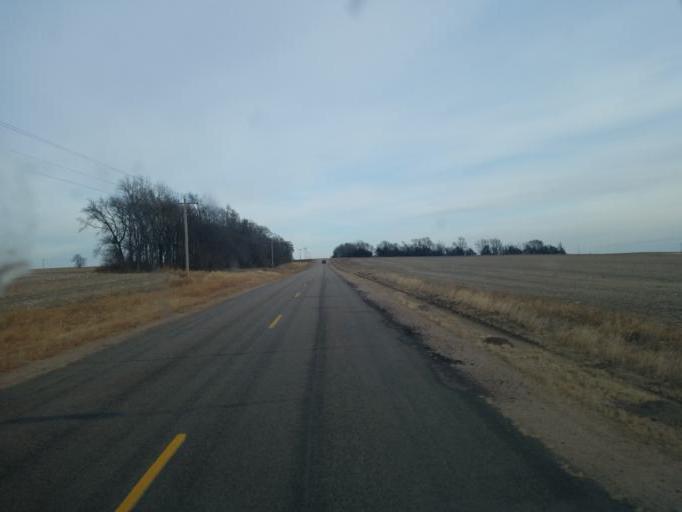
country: US
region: Nebraska
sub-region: Knox County
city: Creighton
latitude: 42.4659
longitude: -98.2732
